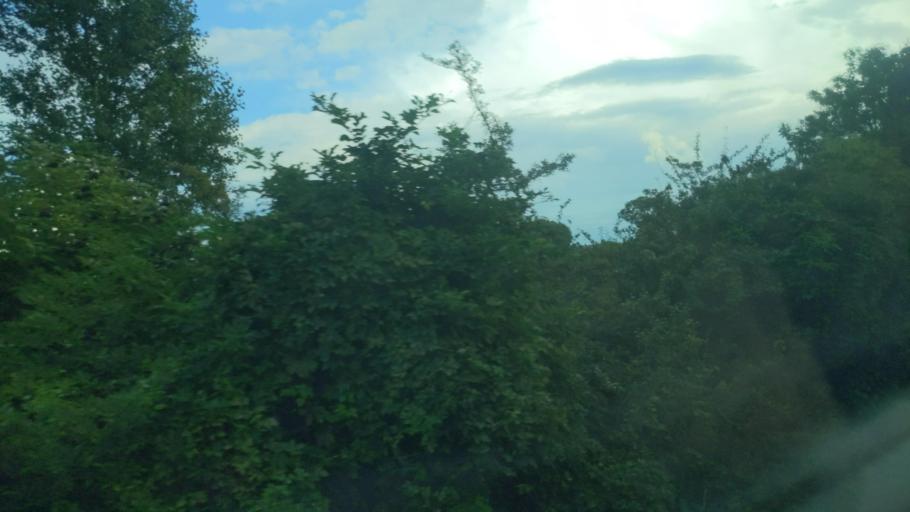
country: CZ
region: Central Bohemia
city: Uvaly
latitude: 50.0782
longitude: 14.7938
